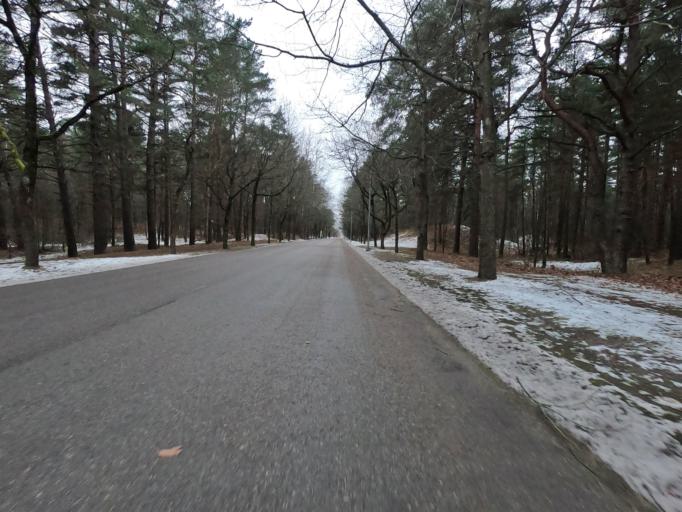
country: LV
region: Riga
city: Jaunciems
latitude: 57.0173
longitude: 24.1432
